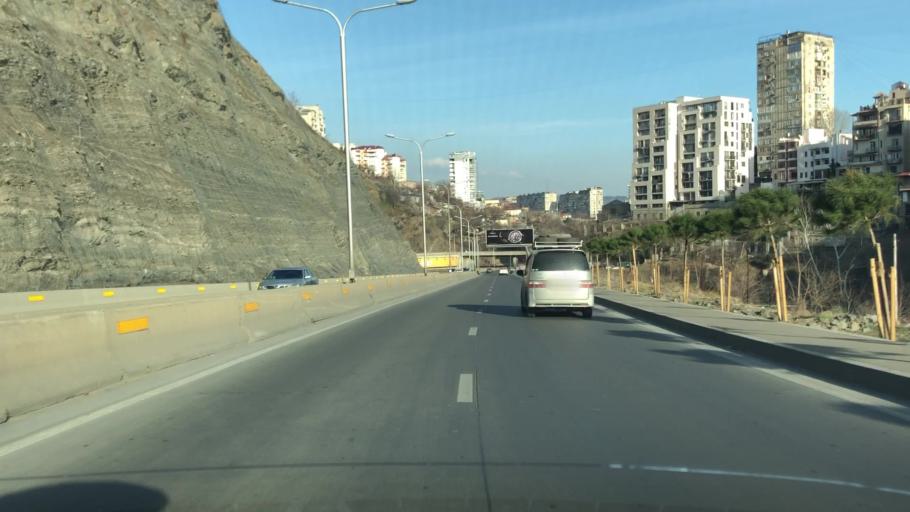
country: GE
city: Tsqnet'i
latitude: 41.7163
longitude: 44.7563
